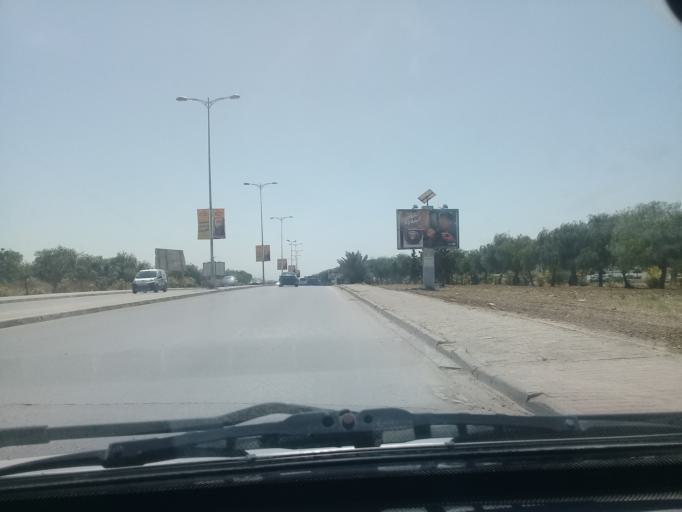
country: TN
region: Tunis
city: La Goulette
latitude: 36.8460
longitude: 10.2584
